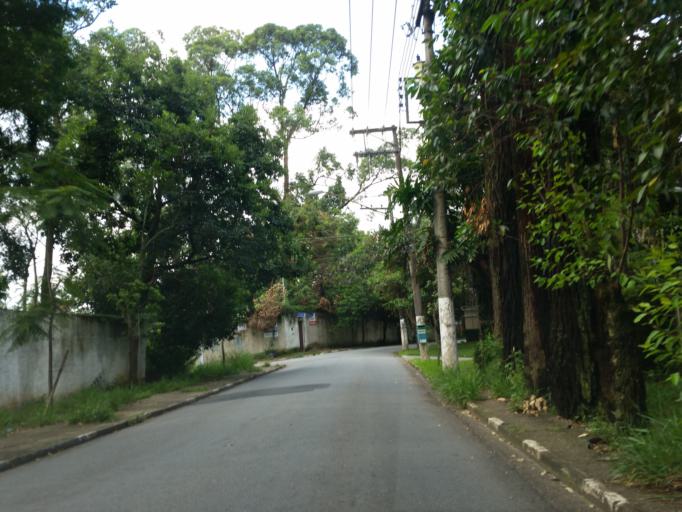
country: BR
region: Sao Paulo
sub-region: Diadema
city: Diadema
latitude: -23.6406
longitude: -46.6820
